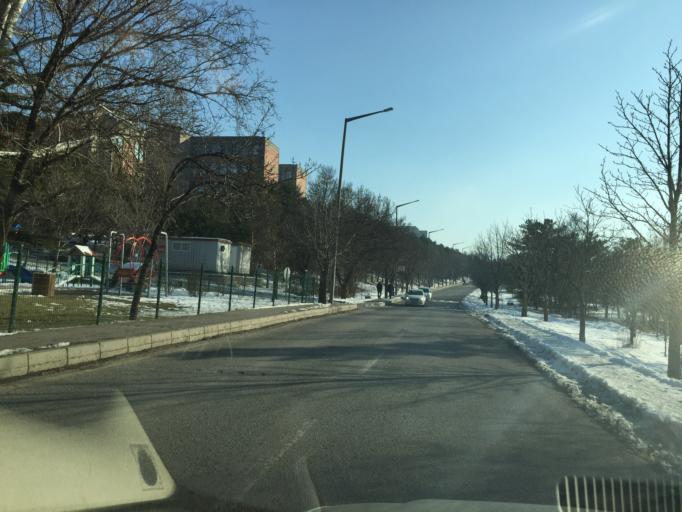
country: TR
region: Ankara
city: Ankara
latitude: 39.8955
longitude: 32.7808
